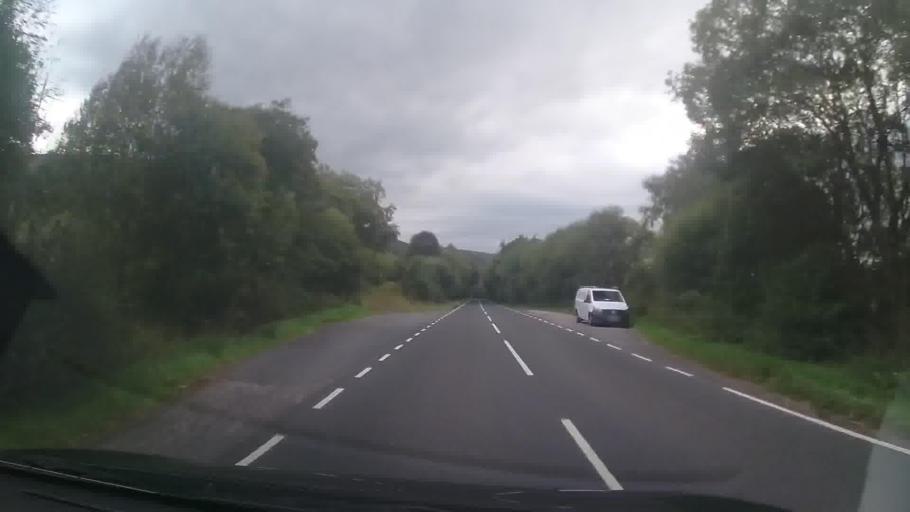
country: GB
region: Scotland
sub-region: Argyll and Bute
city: Garelochhead
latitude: 56.2296
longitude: -4.9769
